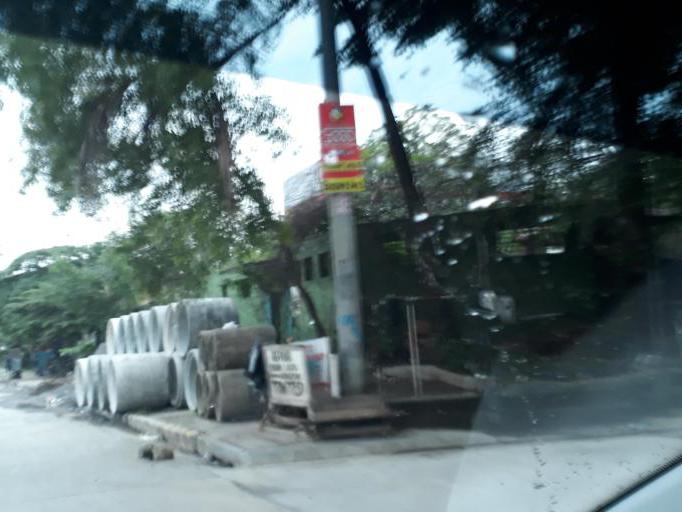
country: PH
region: Calabarzon
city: Del Monte
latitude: 14.6430
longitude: 121.0003
